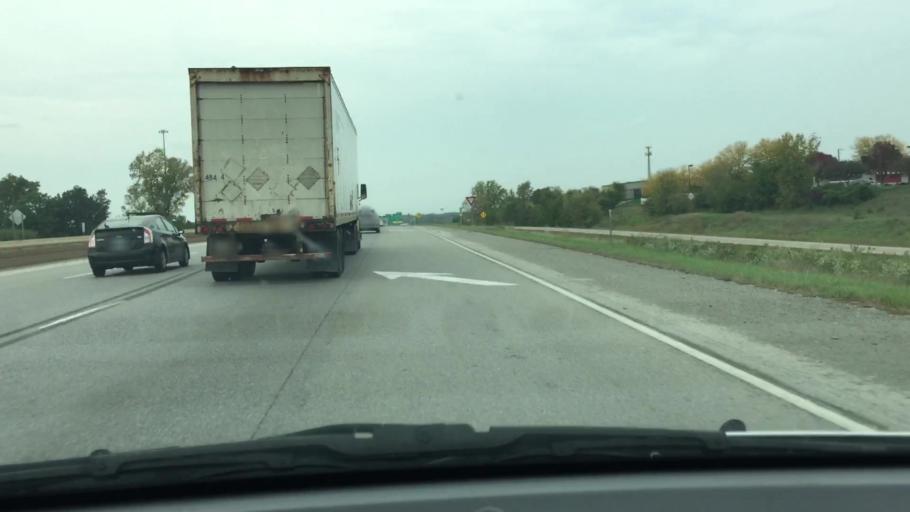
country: US
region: Iowa
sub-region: Johnson County
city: Coralville
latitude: 41.6943
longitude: -91.6103
